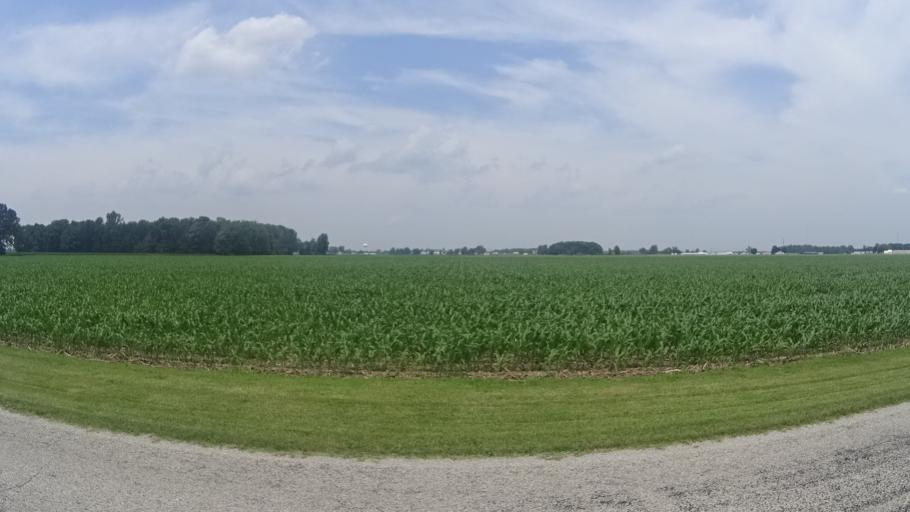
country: US
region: Ohio
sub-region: Erie County
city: Milan
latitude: 41.3076
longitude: -82.6222
